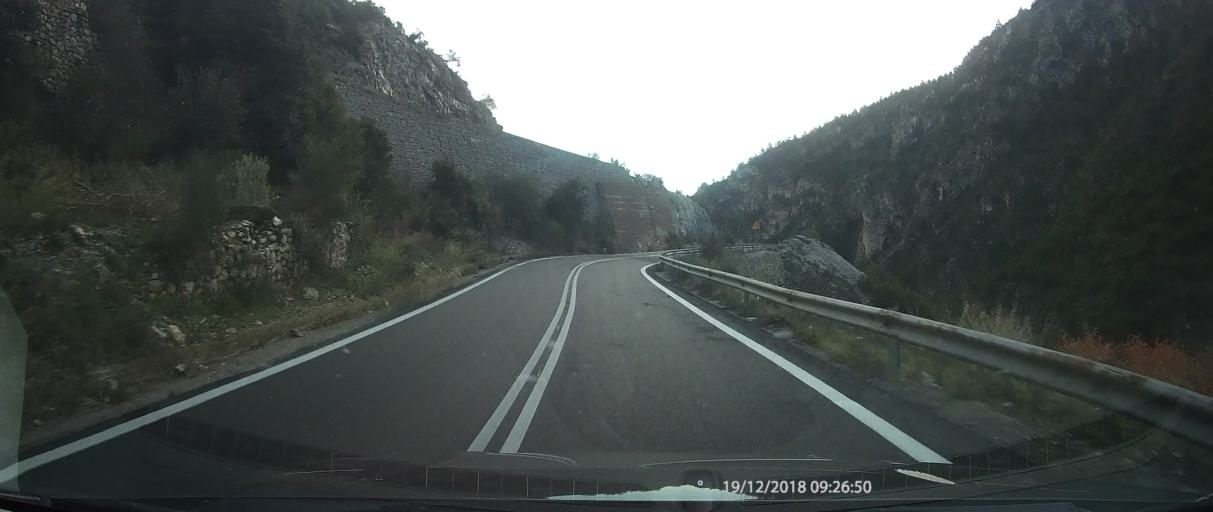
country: GR
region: Peloponnese
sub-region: Nomos Lakonias
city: Magoula
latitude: 37.0933
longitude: 22.3265
